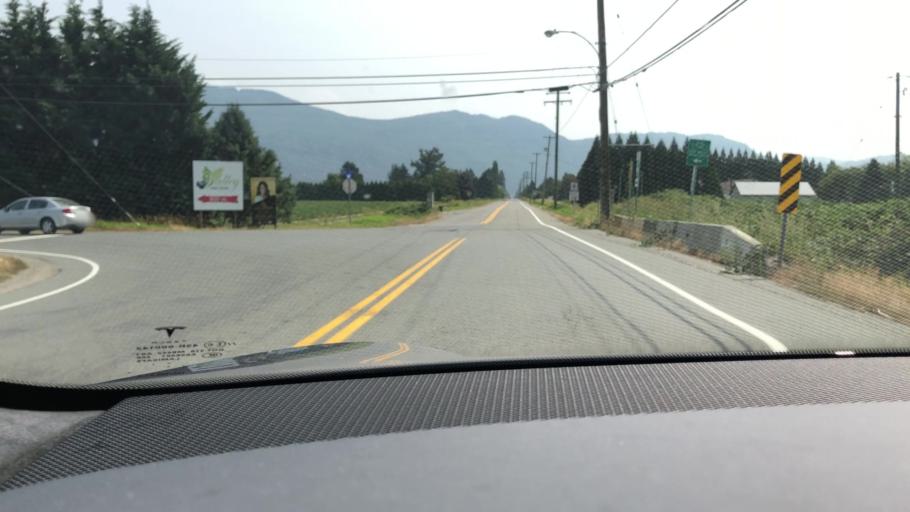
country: US
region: Washington
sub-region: Whatcom County
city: Peaceful Valley
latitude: 49.0896
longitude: -122.0952
